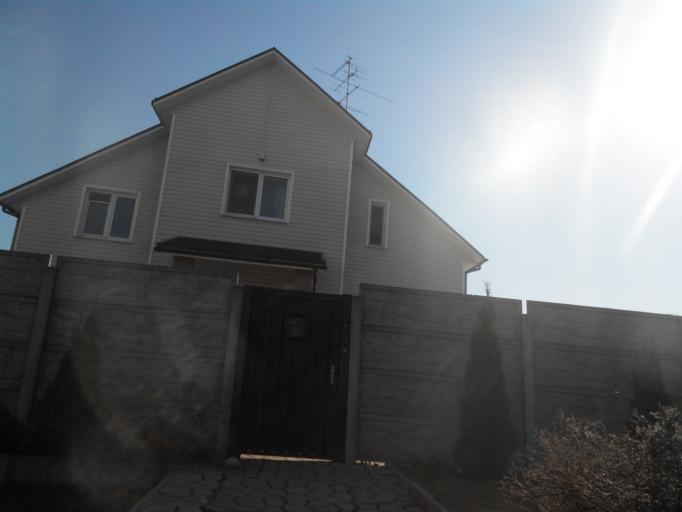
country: BY
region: Minsk
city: Zhdanovichy
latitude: 53.9245
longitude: 27.4079
